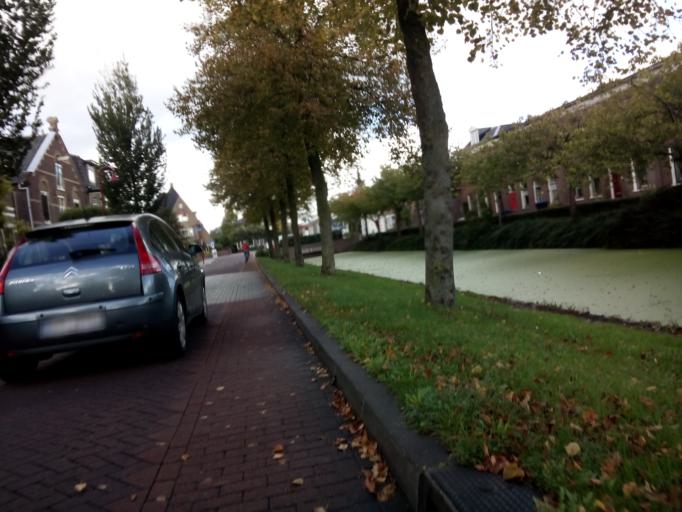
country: NL
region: South Holland
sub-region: Bodegraven-Reeuwijk
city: Bodegraven
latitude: 52.0825
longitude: 4.7504
